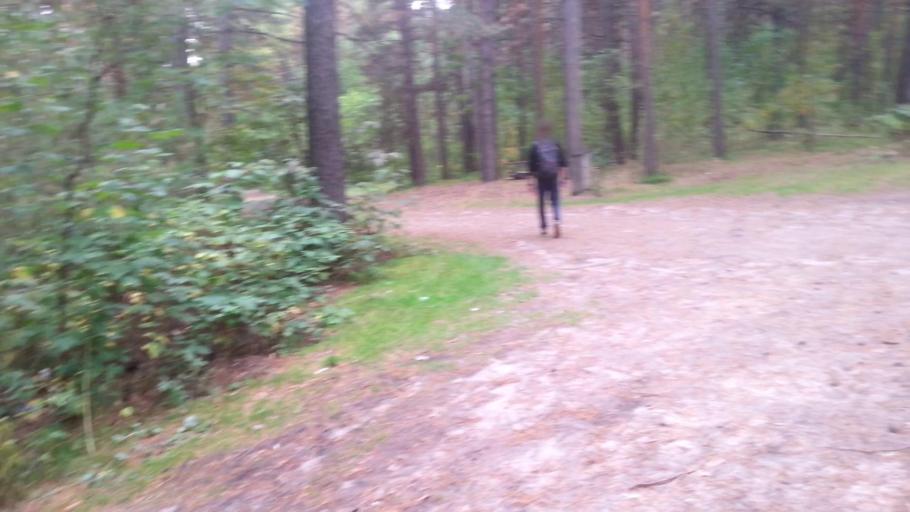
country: RU
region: Altai Krai
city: Yuzhnyy
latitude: 53.3112
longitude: 83.6924
